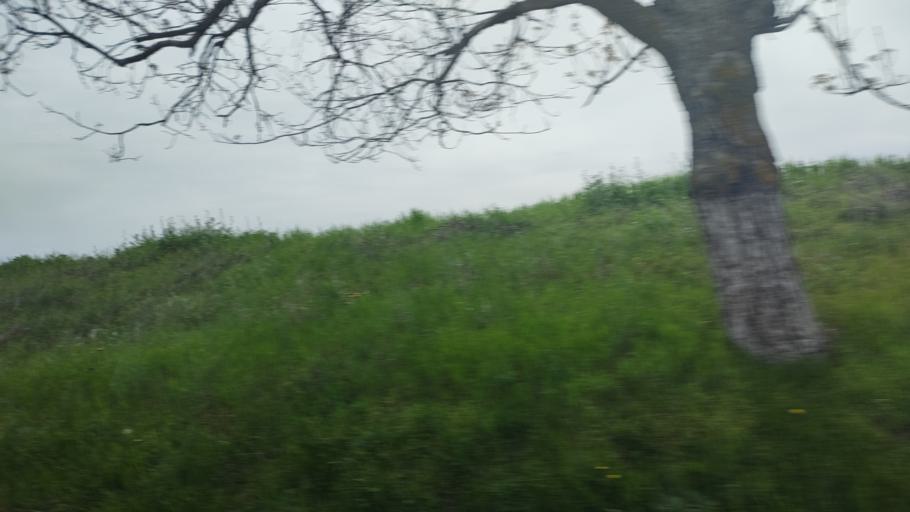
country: RO
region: Constanta
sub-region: Comuna Deleni
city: Pietreni
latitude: 44.0838
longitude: 28.1219
